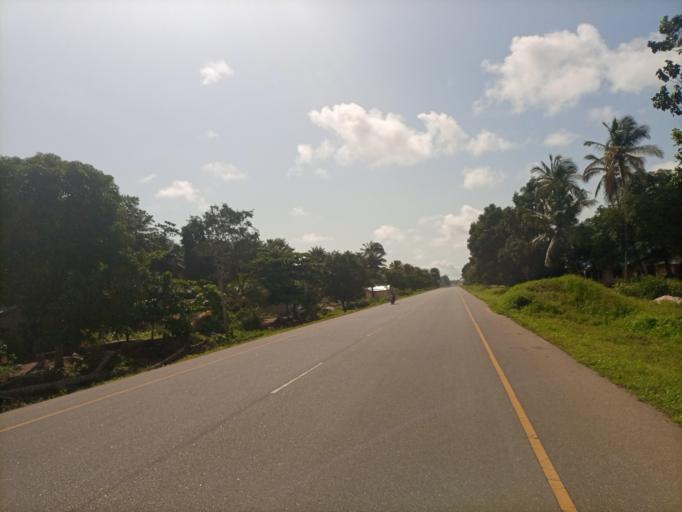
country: SL
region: Northern Province
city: Masoyila
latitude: 8.6251
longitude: -13.1777
